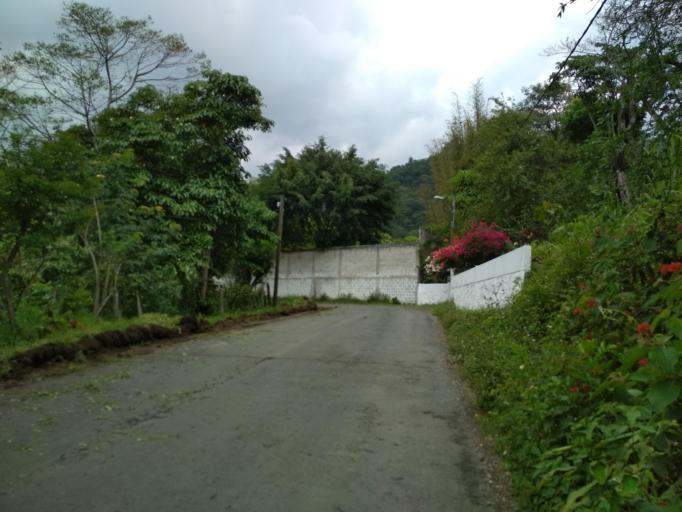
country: MX
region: Veracruz
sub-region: Jilotepec
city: El Pueblito (Garbanzal)
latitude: 19.6177
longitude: -96.9272
